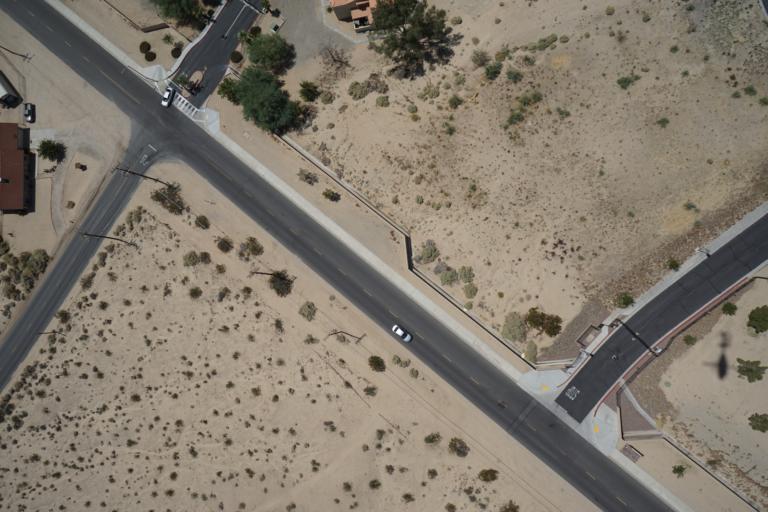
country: US
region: California
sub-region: San Bernardino County
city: Twentynine Palms
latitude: 34.1474
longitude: -116.0456
